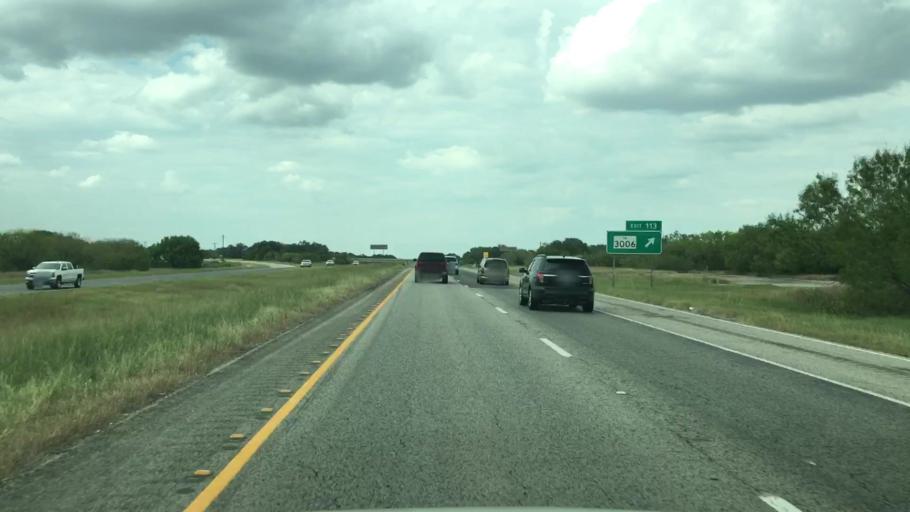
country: US
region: Texas
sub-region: Atascosa County
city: Pleasanton
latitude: 29.0458
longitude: -98.4316
